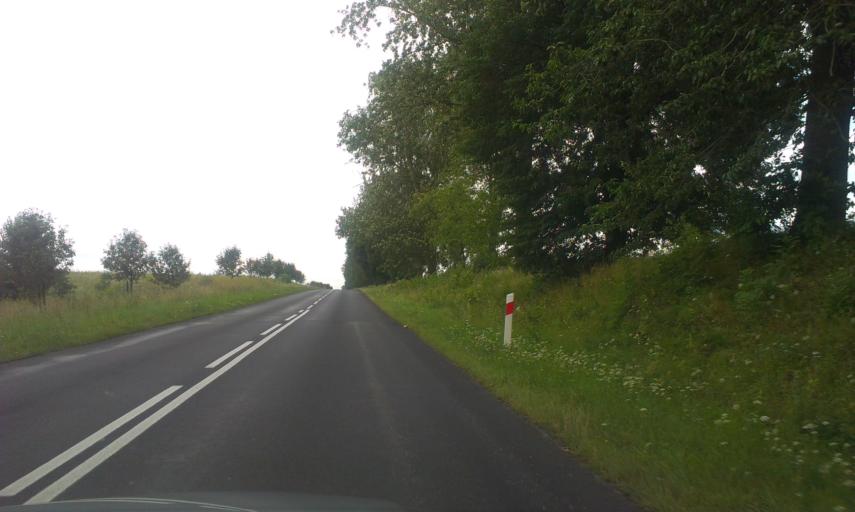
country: PL
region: West Pomeranian Voivodeship
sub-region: Powiat swidwinski
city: Polczyn-Zdroj
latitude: 53.8620
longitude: 16.0703
